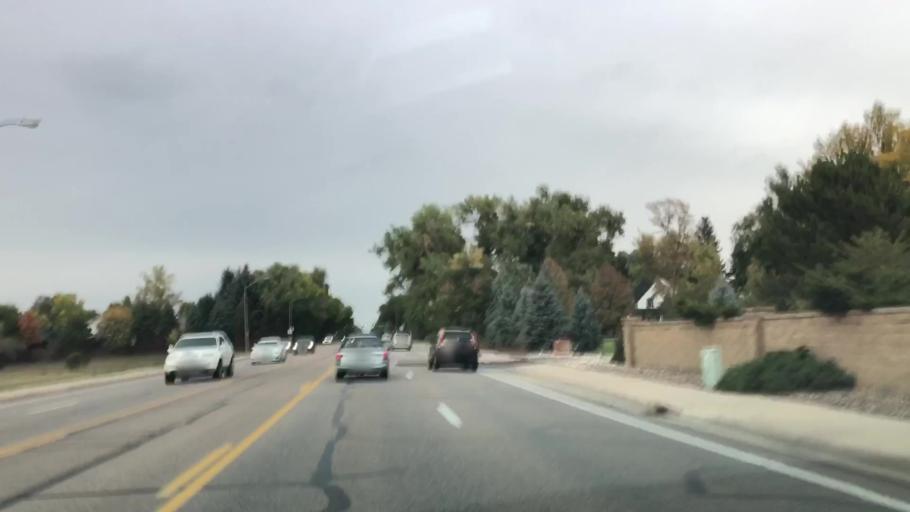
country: US
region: Colorado
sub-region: Larimer County
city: Fort Collins
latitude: 40.5424
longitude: -105.0580
